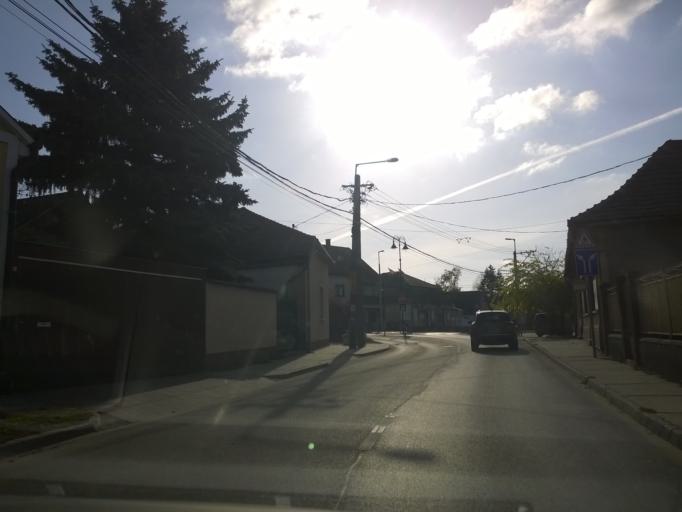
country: HU
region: Pest
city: Rackeve
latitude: 47.1573
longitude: 18.9445
